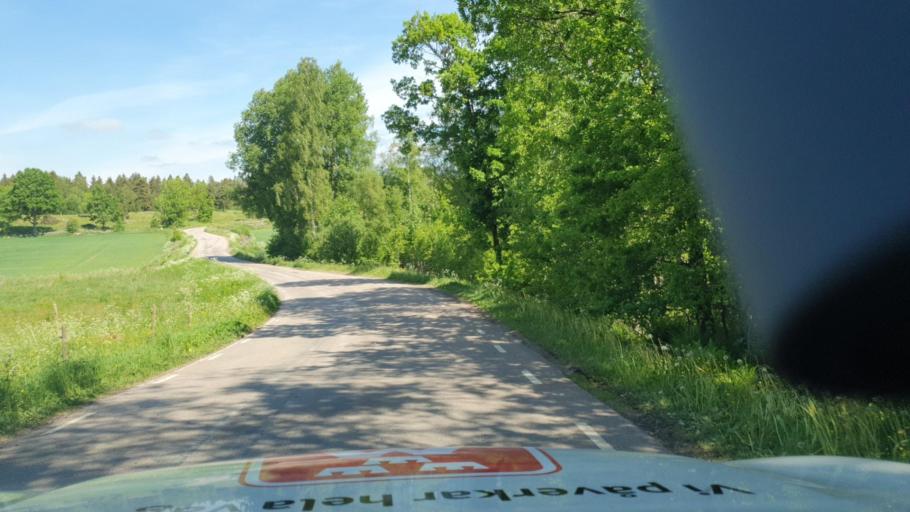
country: SE
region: Vaestra Goetaland
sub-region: Herrljunga Kommun
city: Herrljunga
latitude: 58.0036
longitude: 13.0883
